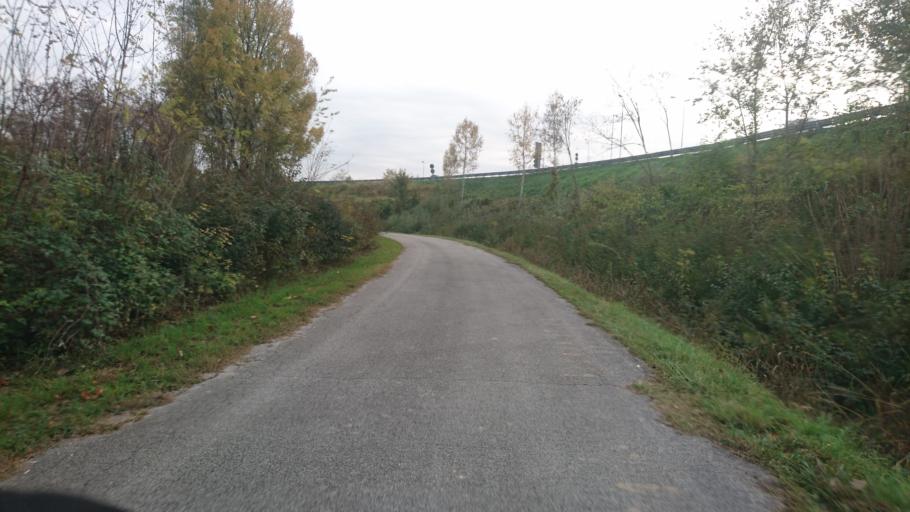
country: IT
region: Veneto
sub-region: Provincia di Padova
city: Tencarola
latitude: 45.3821
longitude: 11.8295
